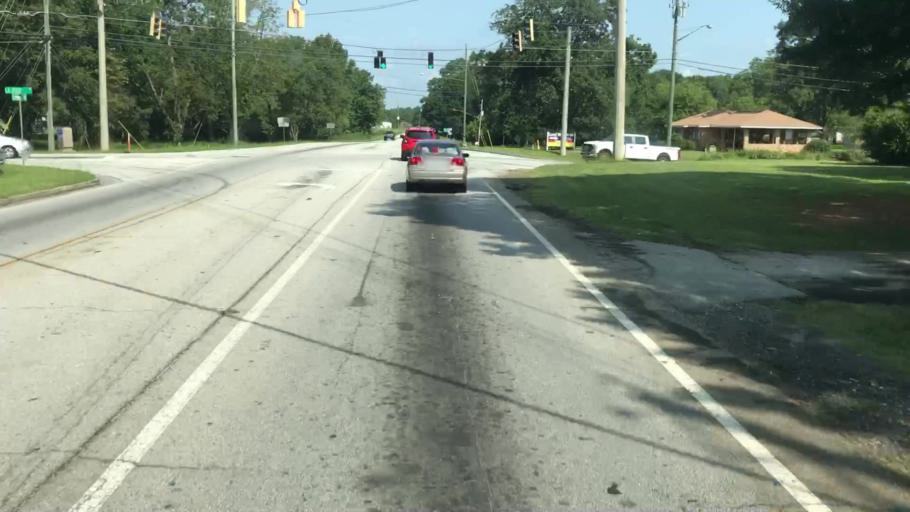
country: US
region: Georgia
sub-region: Walton County
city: Loganville
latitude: 33.8437
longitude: -83.8980
